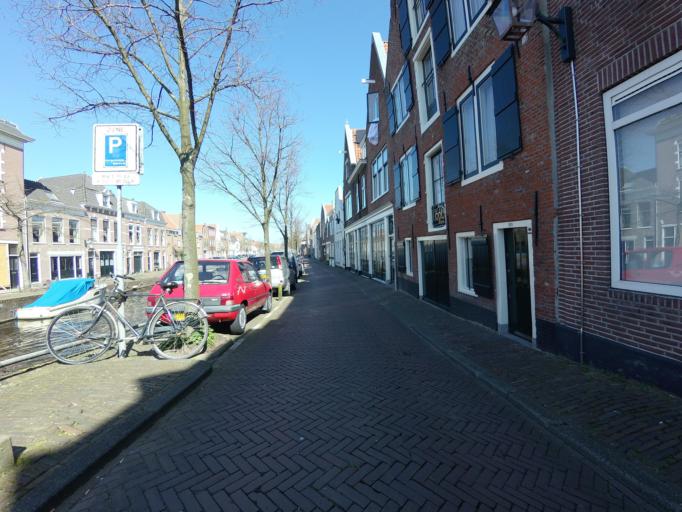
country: NL
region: North Holland
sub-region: Gemeente Haarlem
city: Haarlem
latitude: 52.3772
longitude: 4.6410
